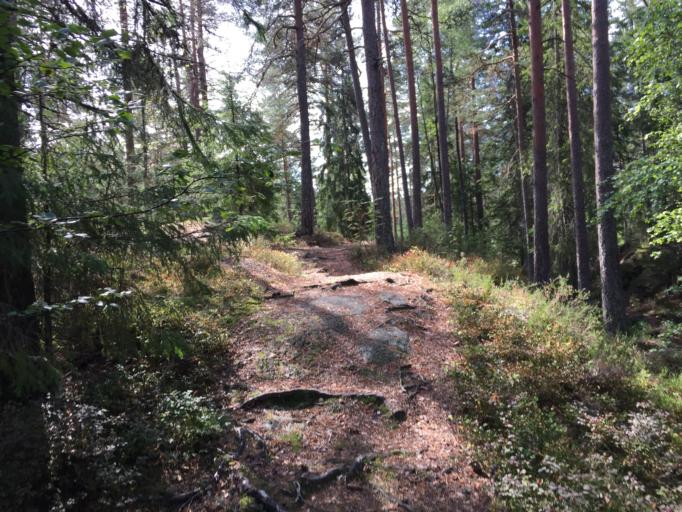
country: NO
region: Akershus
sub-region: Skedsmo
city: Lillestrom
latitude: 59.9278
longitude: 11.0212
